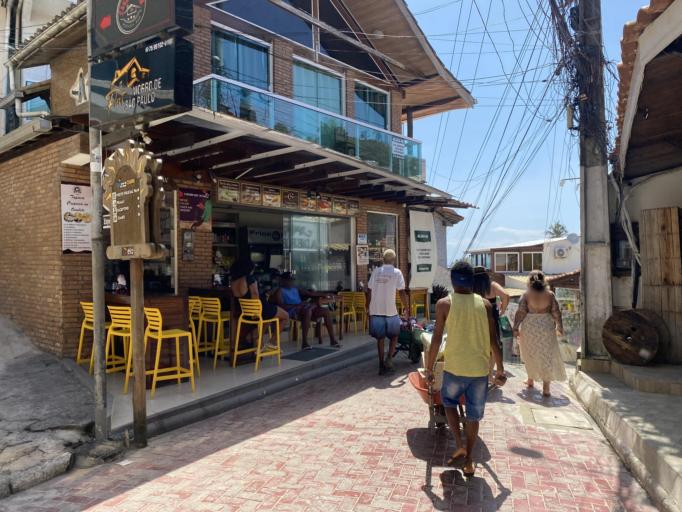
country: BR
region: Bahia
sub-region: Valenca
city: Valenca
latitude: -13.3777
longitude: -38.9150
